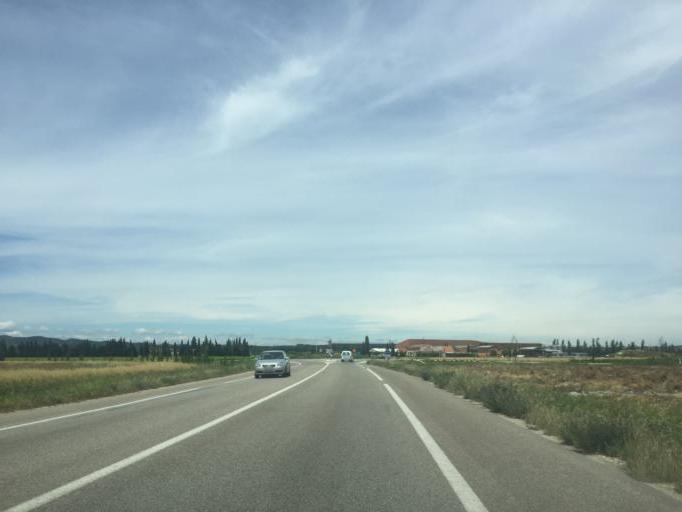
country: FR
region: Languedoc-Roussillon
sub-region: Departement du Gard
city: Les Angles
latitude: 43.9864
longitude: 4.7481
